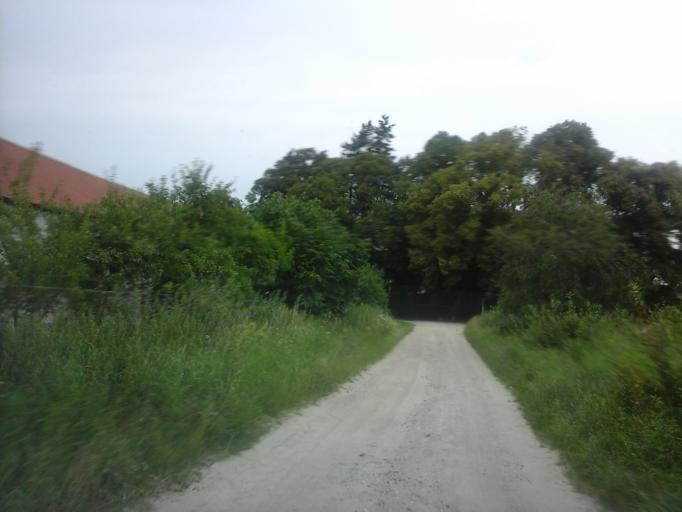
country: PL
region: West Pomeranian Voivodeship
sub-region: Powiat choszczenski
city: Recz
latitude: 53.2571
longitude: 15.5567
